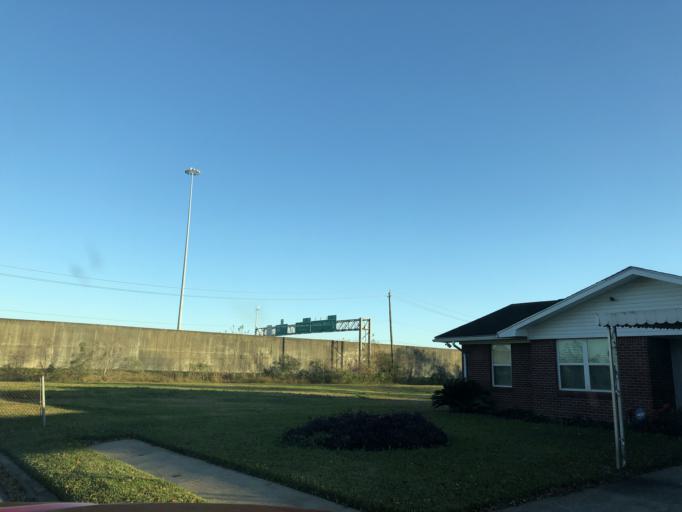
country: US
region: Texas
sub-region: Harris County
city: Jacinto City
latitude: 29.7611
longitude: -95.2663
